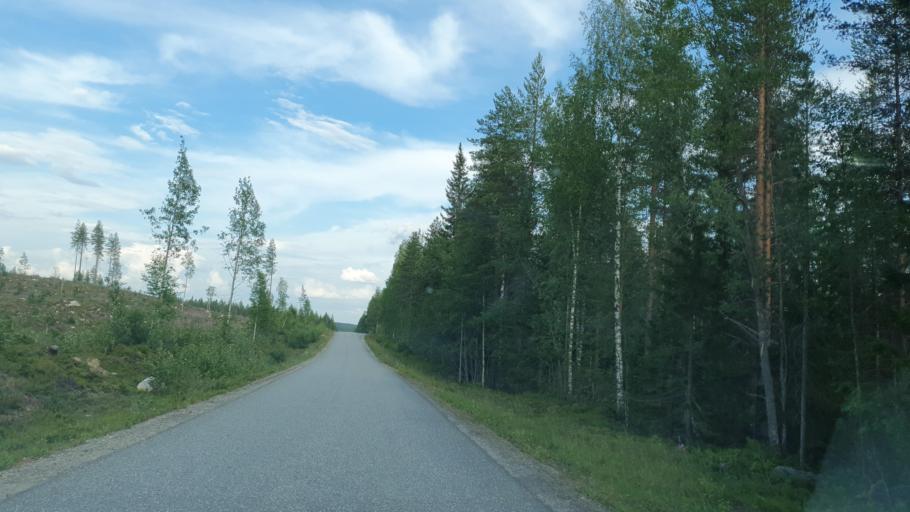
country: FI
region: Kainuu
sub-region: Kehys-Kainuu
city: Kuhmo
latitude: 64.2821
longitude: 29.3989
